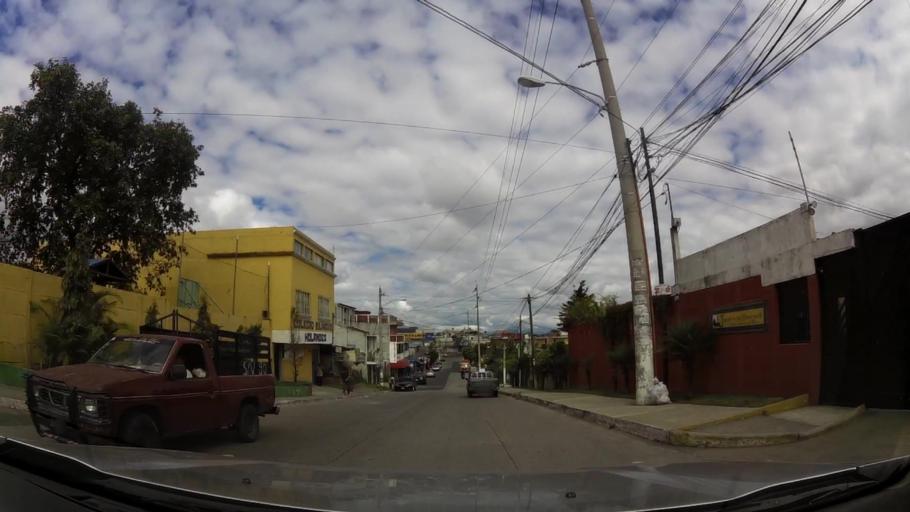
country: GT
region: Guatemala
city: Guatemala City
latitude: 14.6751
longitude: -90.5477
